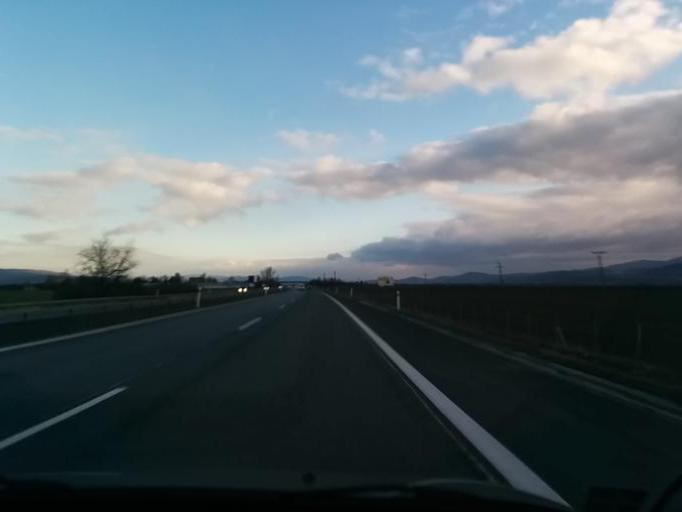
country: SK
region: Trnavsky
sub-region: Okres Trnava
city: Piestany
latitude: 48.6231
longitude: 17.8052
